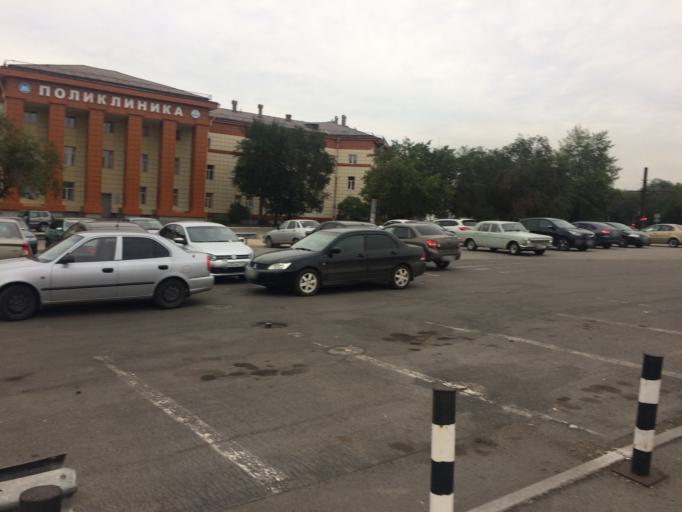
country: RU
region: Chelyabinsk
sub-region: Gorod Magnitogorsk
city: Magnitogorsk
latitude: 53.4157
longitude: 59.0571
